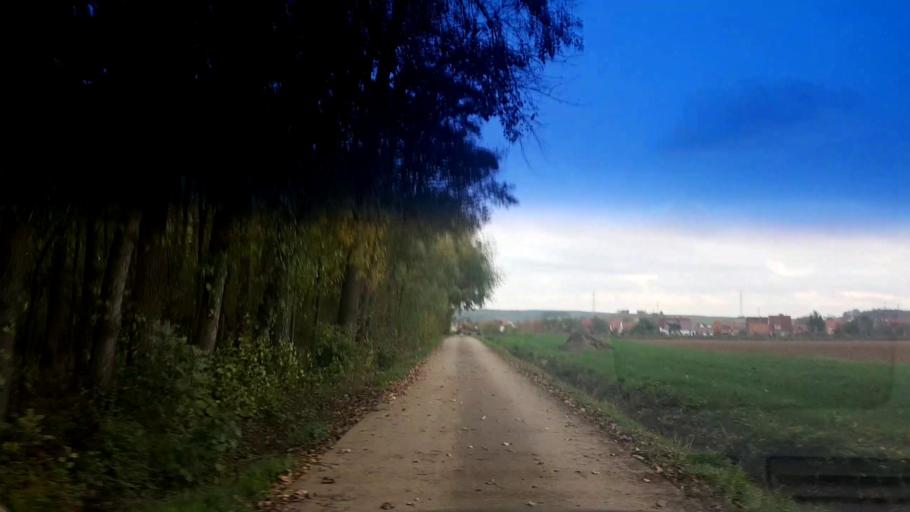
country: DE
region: Bavaria
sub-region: Upper Franconia
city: Memmelsdorf
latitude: 49.9636
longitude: 10.9600
